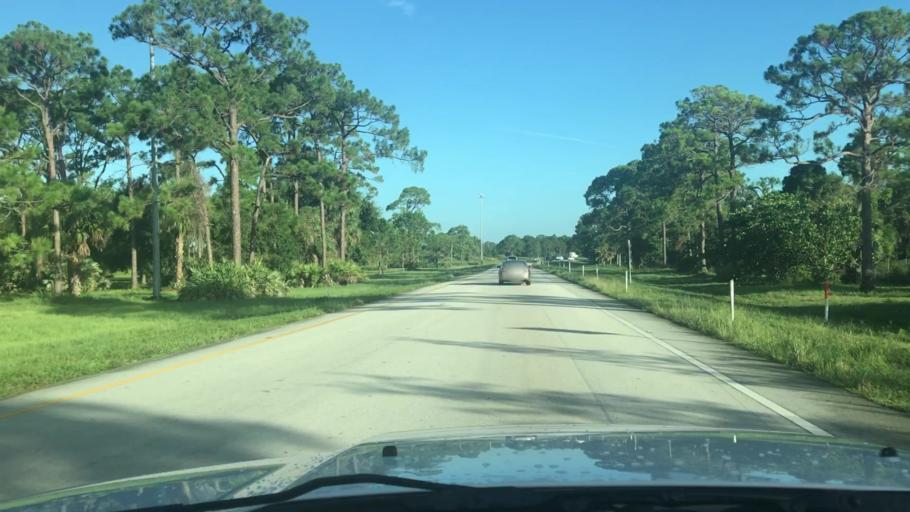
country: US
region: Florida
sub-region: Martin County
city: Palm City
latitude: 27.1625
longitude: -80.3877
